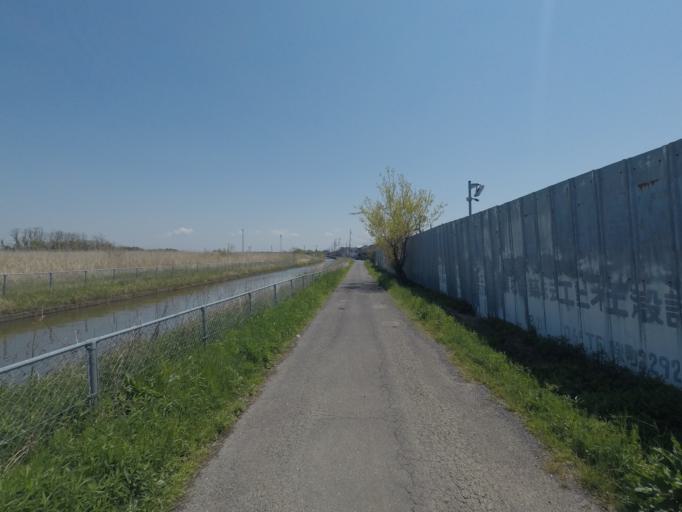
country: JP
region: Ibaraki
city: Fujishiro
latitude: 35.9412
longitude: 140.1201
